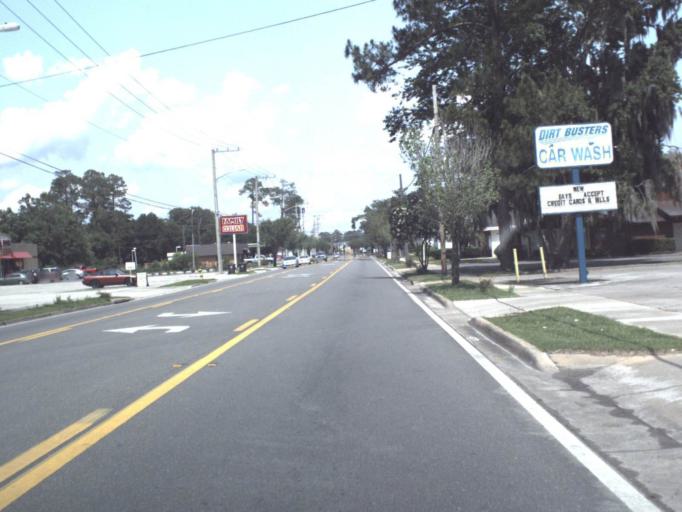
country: US
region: Florida
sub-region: Baker County
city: Macclenny
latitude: 30.2814
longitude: -82.1291
